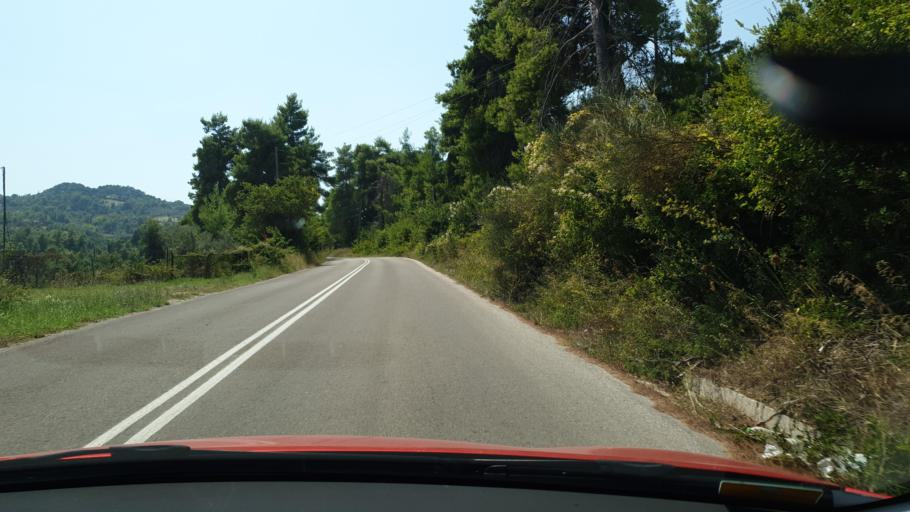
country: GR
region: Central Greece
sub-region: Nomos Evvoias
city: Oxilithos
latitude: 38.5977
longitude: 24.0756
